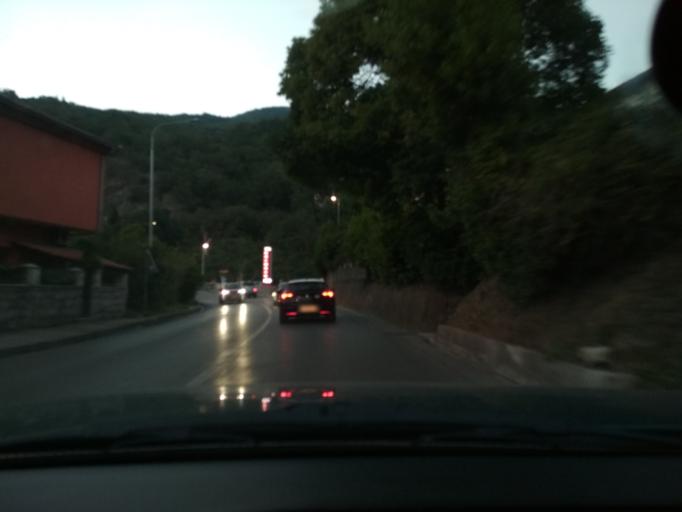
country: ME
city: Igalo
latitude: 42.4611
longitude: 18.5207
